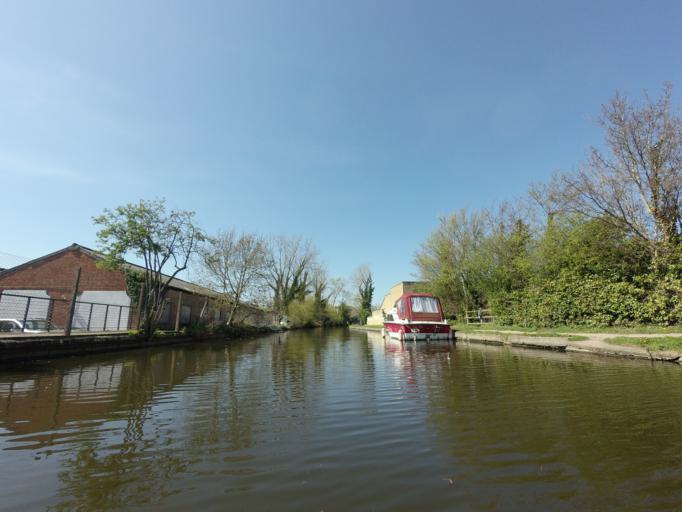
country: GB
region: England
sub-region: Greater London
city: West Drayton
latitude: 51.5123
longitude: -0.4751
